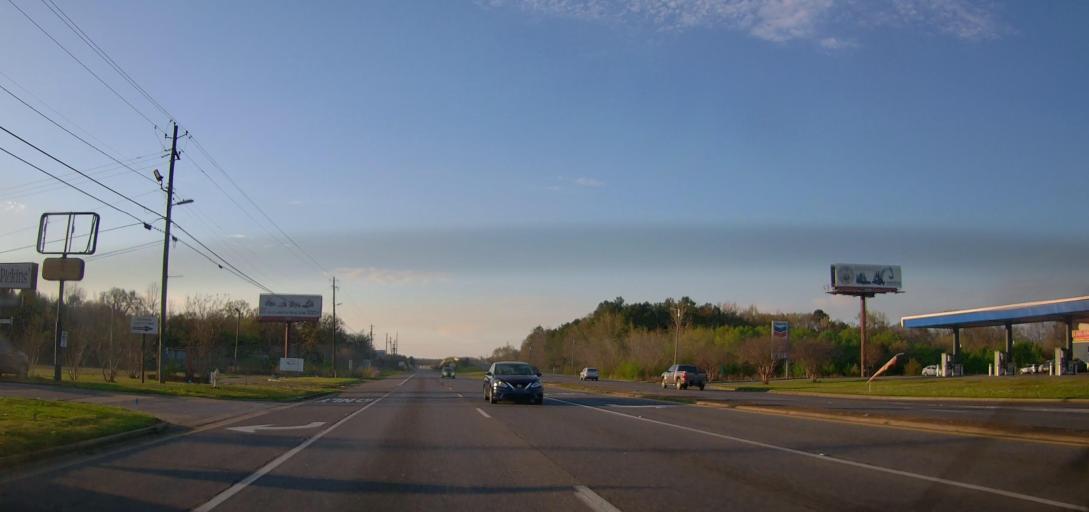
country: US
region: Alabama
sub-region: Talladega County
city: Childersburg
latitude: 33.2855
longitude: -86.3630
